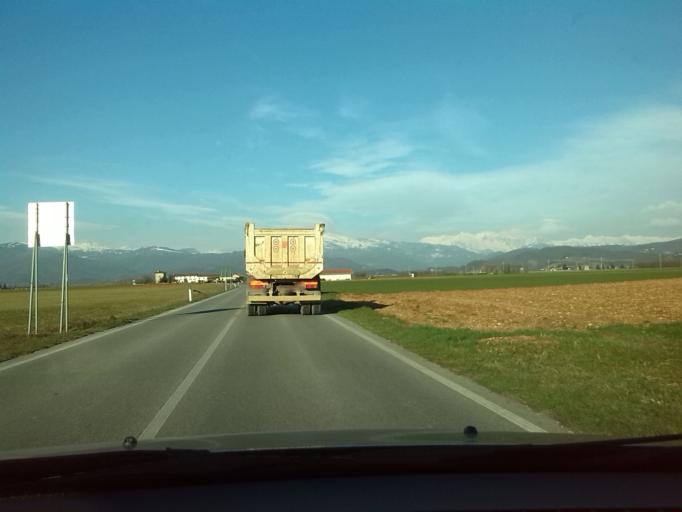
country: IT
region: Friuli Venezia Giulia
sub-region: Provincia di Udine
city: Premariacco
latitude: 46.0479
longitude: 13.4081
